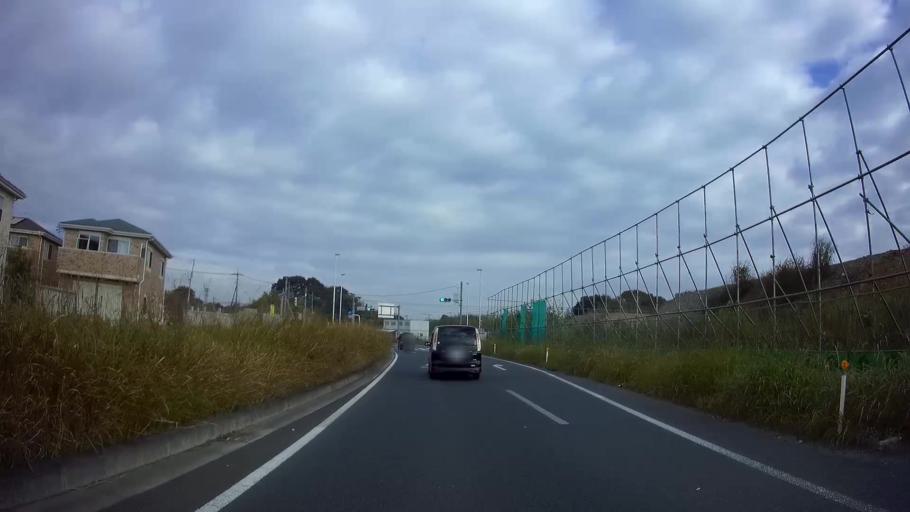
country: JP
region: Saitama
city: Okegawa
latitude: 36.0039
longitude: 139.5182
